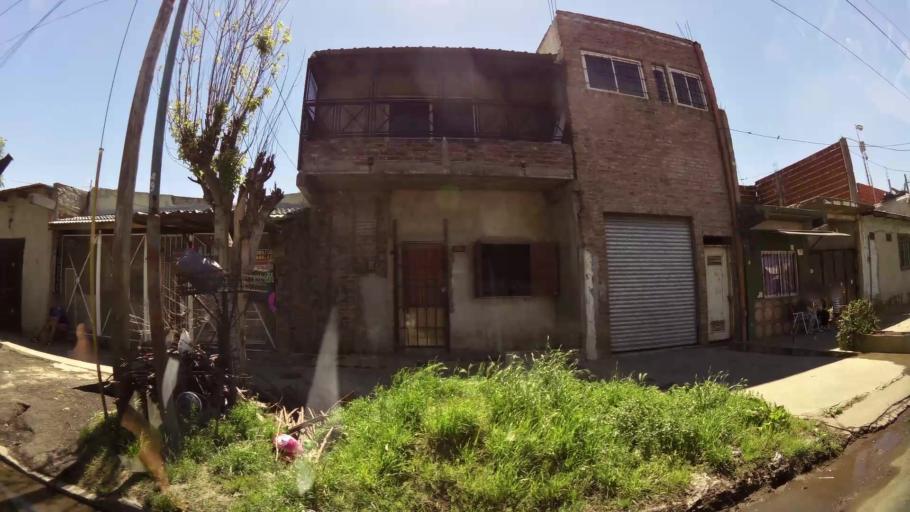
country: AR
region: Buenos Aires
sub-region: Partido de Lanus
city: Lanus
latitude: -34.7268
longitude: -58.3333
